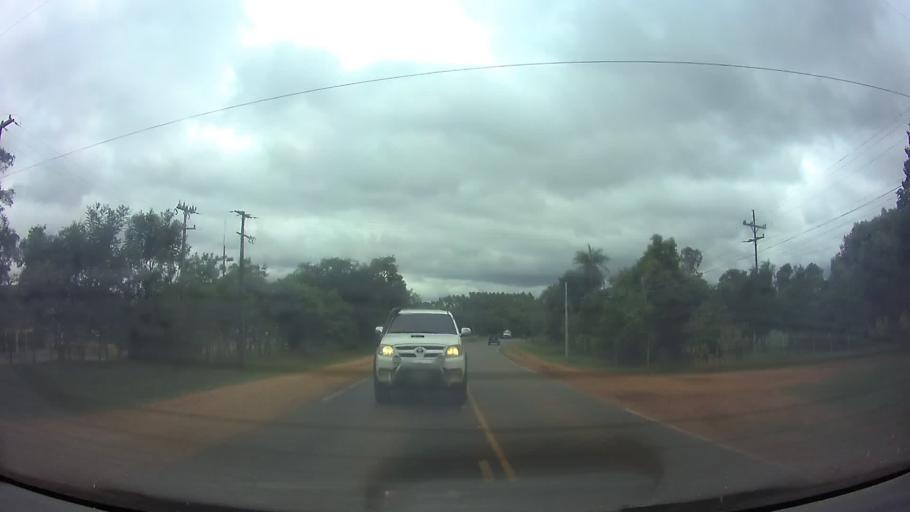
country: PY
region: Central
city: Guarambare
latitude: -25.5128
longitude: -57.4891
